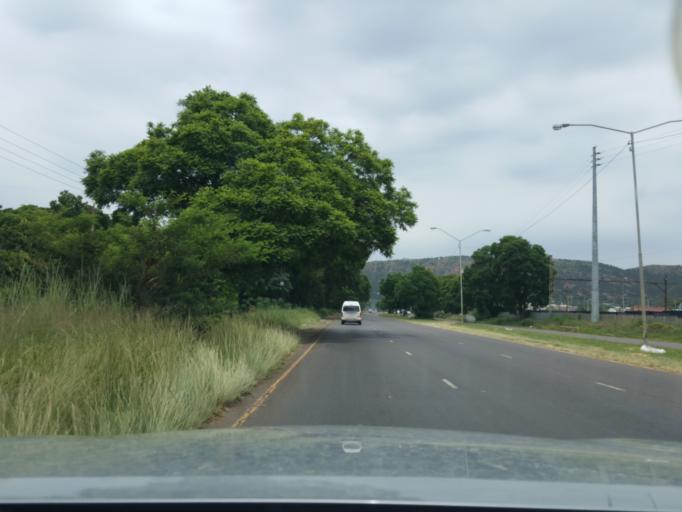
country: ZA
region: Gauteng
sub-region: City of Tshwane Metropolitan Municipality
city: Pretoria
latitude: -25.6709
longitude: 28.1829
